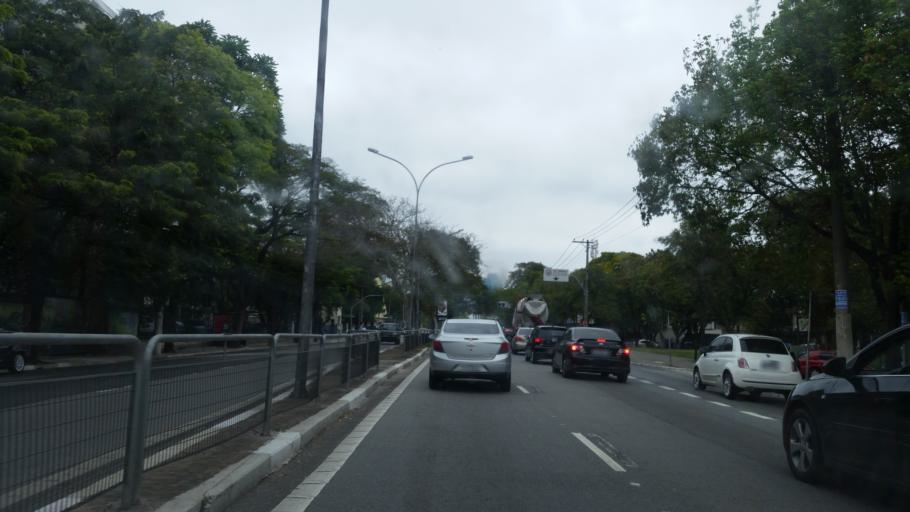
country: BR
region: Sao Paulo
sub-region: Sao Paulo
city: Sao Paulo
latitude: -23.5946
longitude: -46.6538
